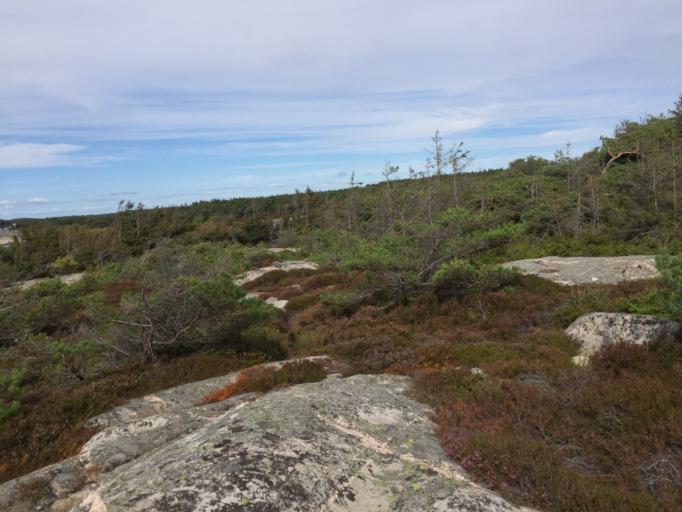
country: NO
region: Ostfold
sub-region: Hvaler
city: Skjaerhalden
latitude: 59.0210
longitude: 11.0143
